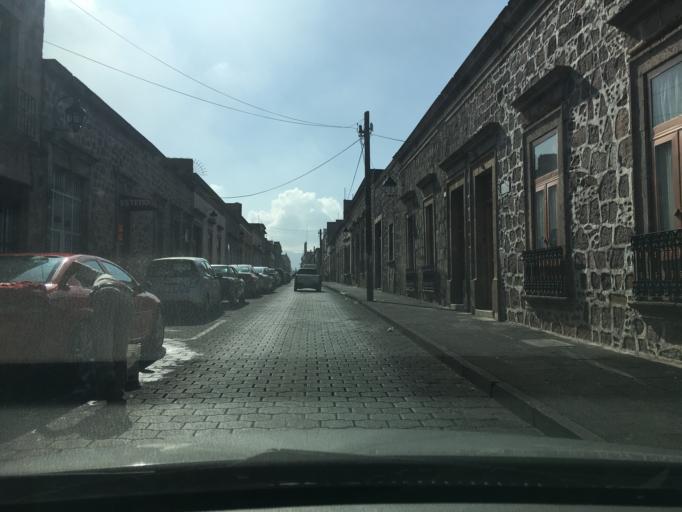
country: MX
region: Michoacan
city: Morelia
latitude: 19.7020
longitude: -101.1979
